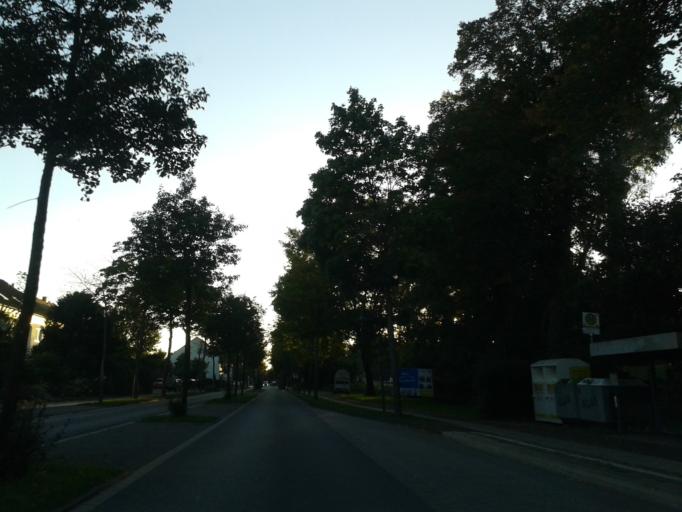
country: DE
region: North Rhine-Westphalia
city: Bad Lippspringe
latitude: 51.7669
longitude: 8.7945
